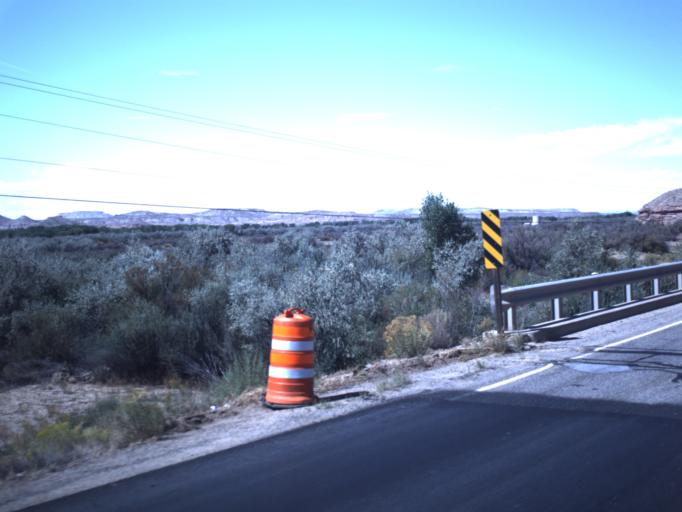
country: US
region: Colorado
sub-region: Montezuma County
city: Towaoc
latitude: 37.2181
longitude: -109.1903
